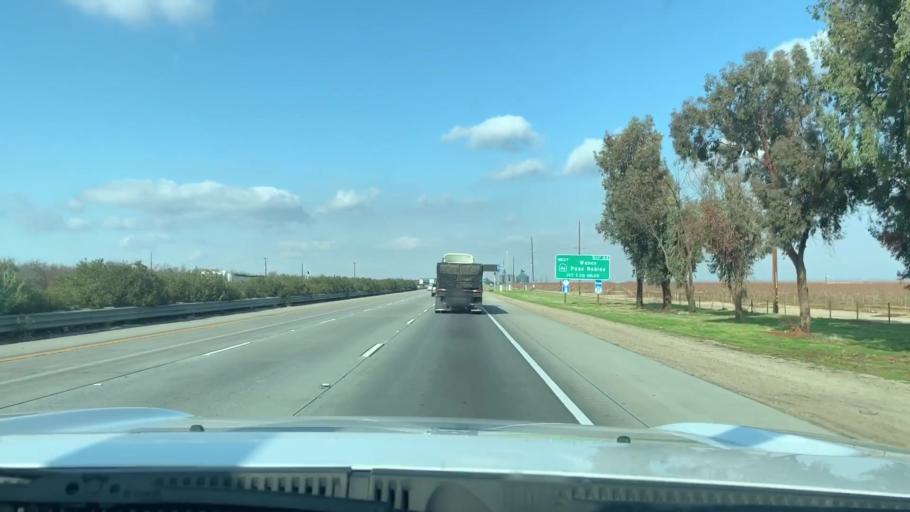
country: US
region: California
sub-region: Kern County
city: McFarland
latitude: 35.5780
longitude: -119.2026
